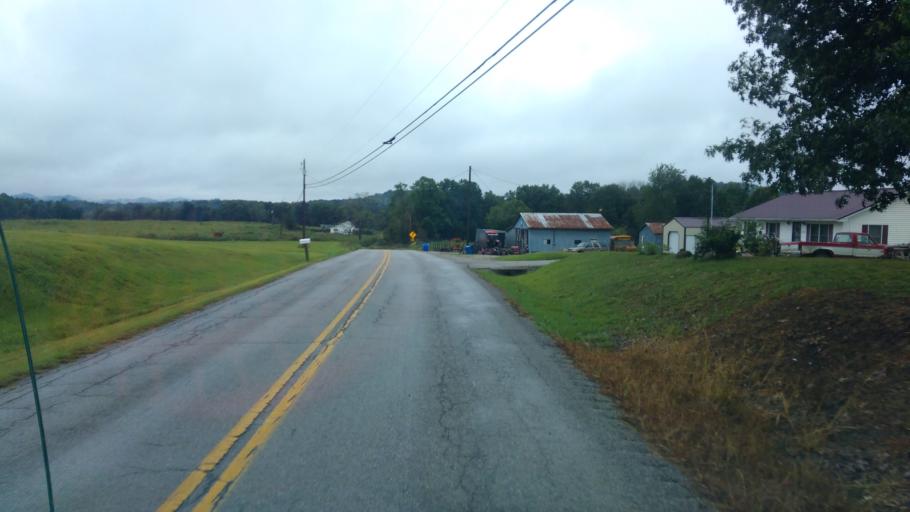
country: US
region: Kentucky
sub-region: Fleming County
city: Flemingsburg
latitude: 38.4560
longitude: -83.5215
